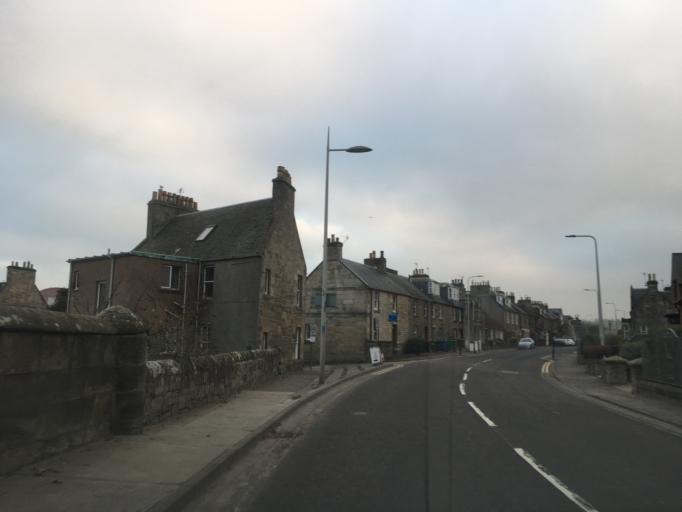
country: GB
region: Scotland
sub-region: Fife
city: Saint Andrews
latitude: 56.3362
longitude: -2.7844
